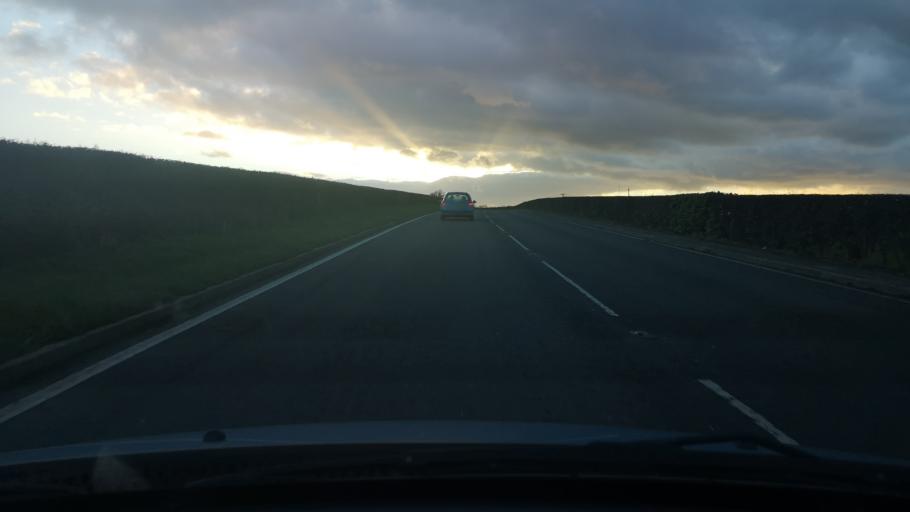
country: GB
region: England
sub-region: City and Borough of Wakefield
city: Horbury
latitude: 53.6284
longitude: -1.5697
